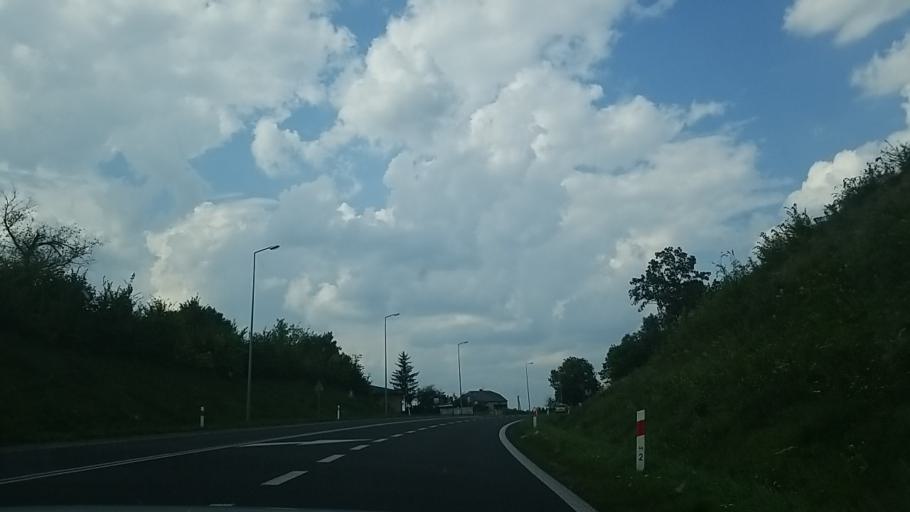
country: PL
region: Lublin Voivodeship
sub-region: Powiat bilgorajski
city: Goraj
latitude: 50.7282
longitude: 22.6671
